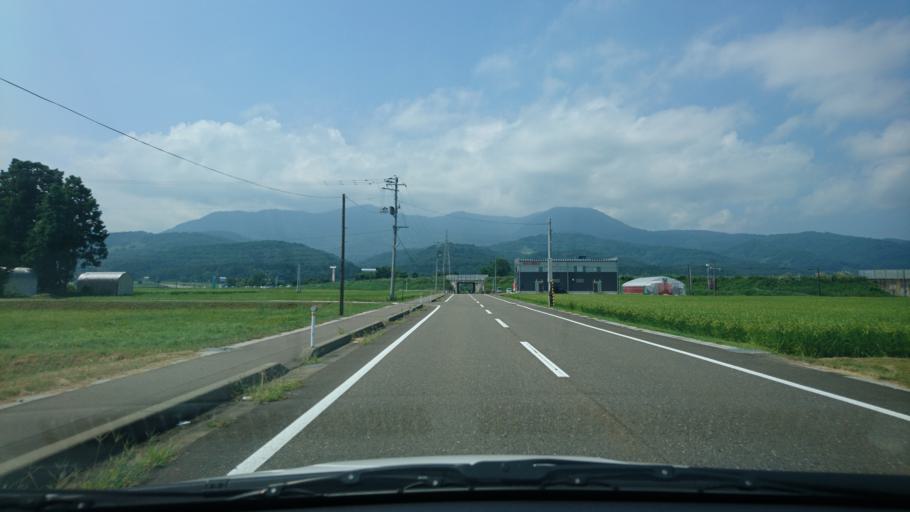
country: JP
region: Niigata
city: Arai
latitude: 37.0507
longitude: 138.2503
